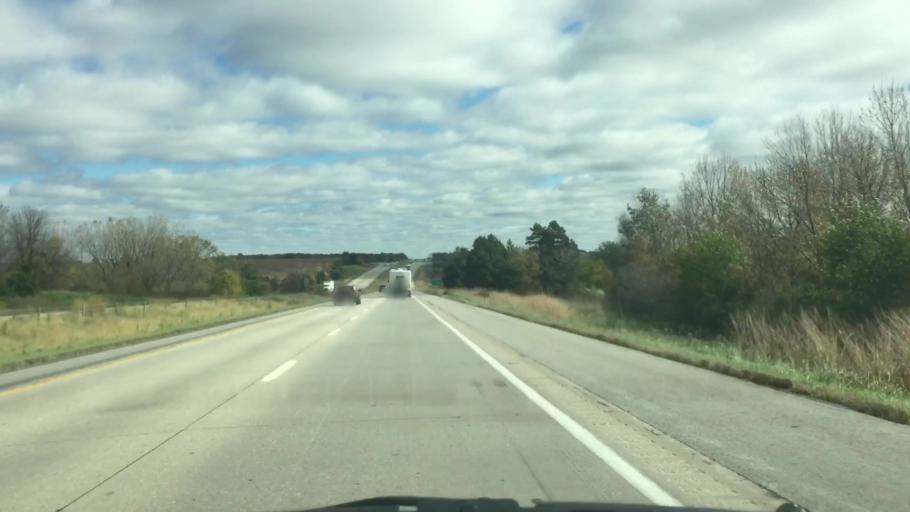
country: US
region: Iowa
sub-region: Jasper County
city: Newton
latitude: 41.6829
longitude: -93.0178
